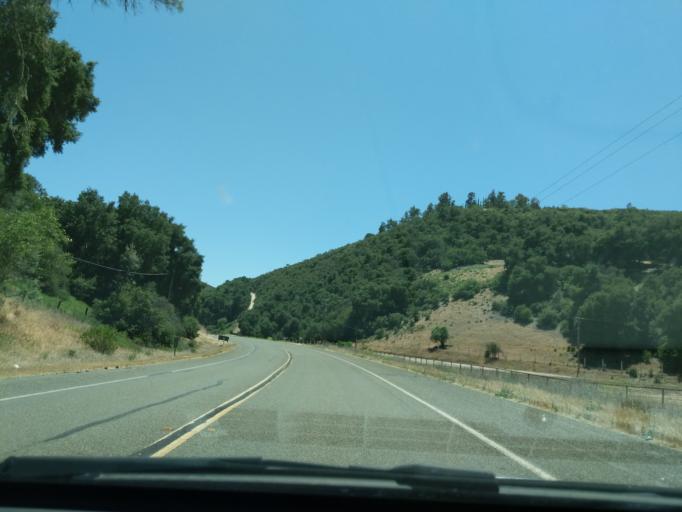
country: US
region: California
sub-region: Monterey County
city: King City
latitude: 36.0694
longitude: -121.1837
